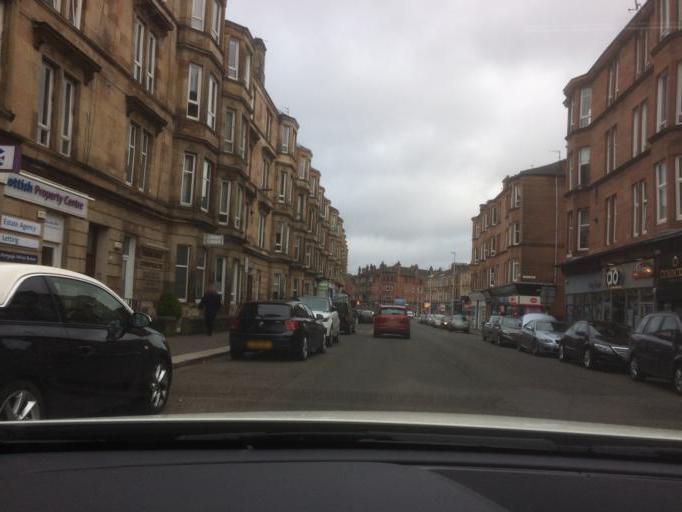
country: GB
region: Scotland
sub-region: East Renfrewshire
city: Giffnock
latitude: 55.8273
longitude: -4.2846
